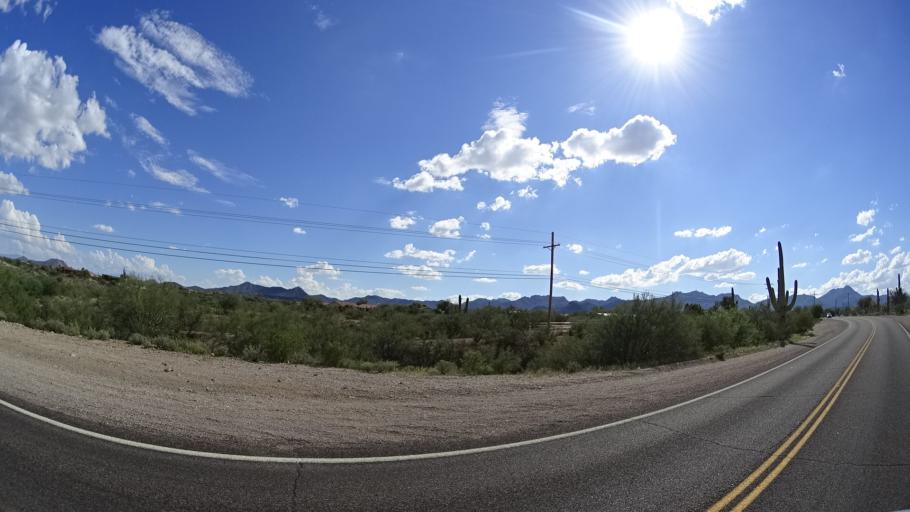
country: US
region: Arizona
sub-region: Pima County
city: Flowing Wells
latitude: 32.2800
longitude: -111.0479
